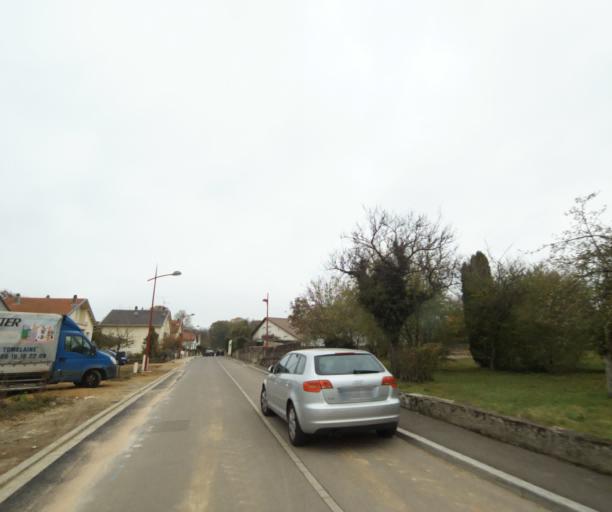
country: FR
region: Lorraine
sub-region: Departement de Meurthe-et-Moselle
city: Moutiers
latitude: 49.2365
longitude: 5.9725
